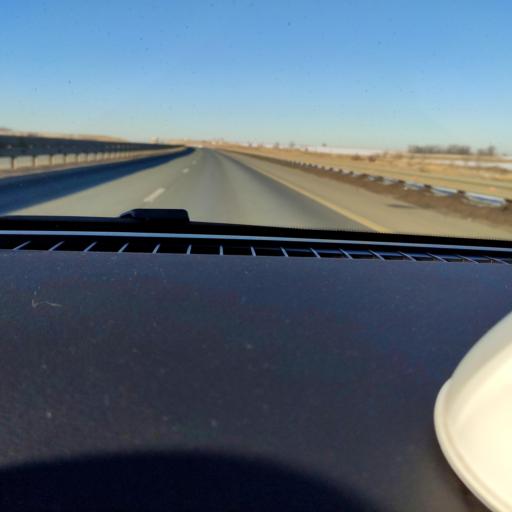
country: RU
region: Samara
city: Smyshlyayevka
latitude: 53.1441
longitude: 50.4125
